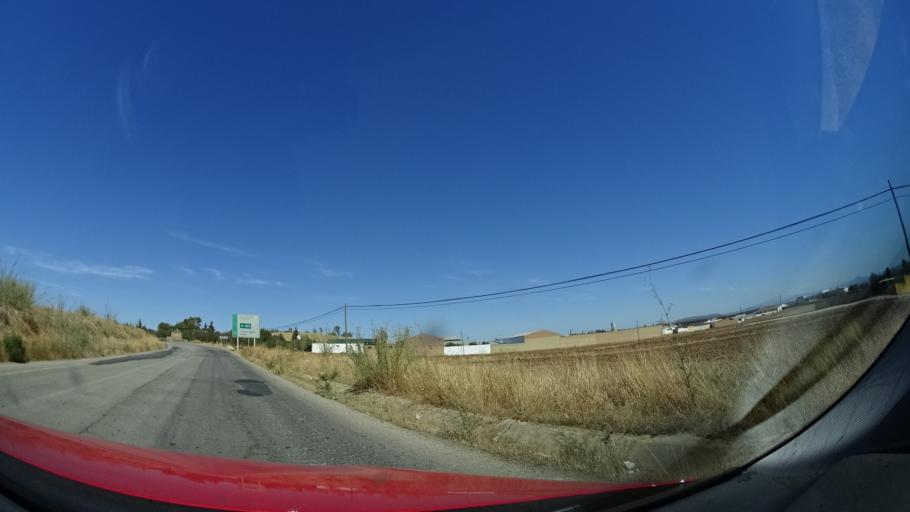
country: ES
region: Andalusia
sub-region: Provincia de Malaga
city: Campillos
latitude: 37.0558
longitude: -4.8640
